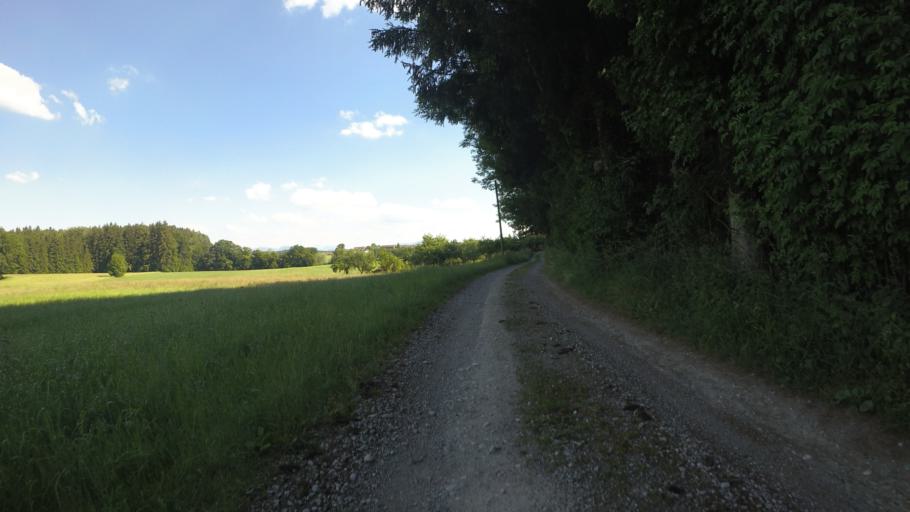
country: DE
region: Bavaria
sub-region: Upper Bavaria
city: Seeon-Seebruck
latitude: 47.9654
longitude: 12.5048
